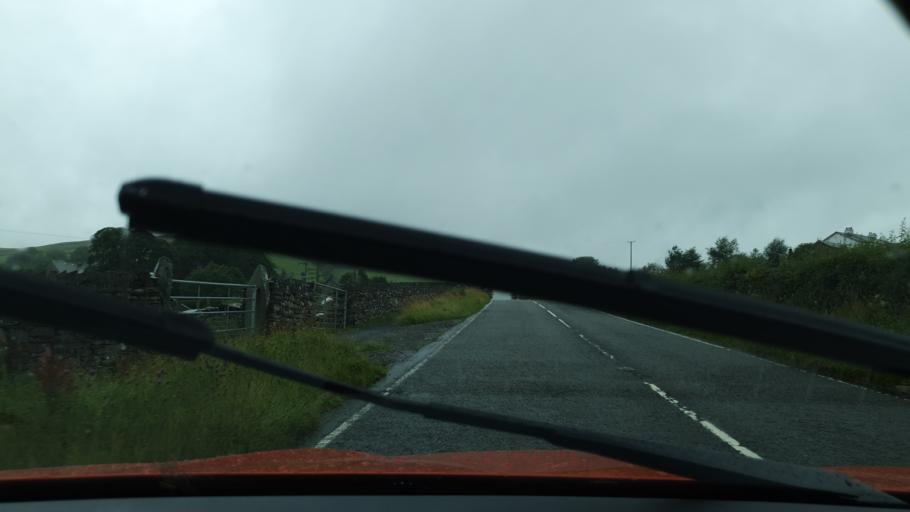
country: GB
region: England
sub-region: Cumbria
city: Ulverston
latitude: 54.2552
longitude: -3.1165
